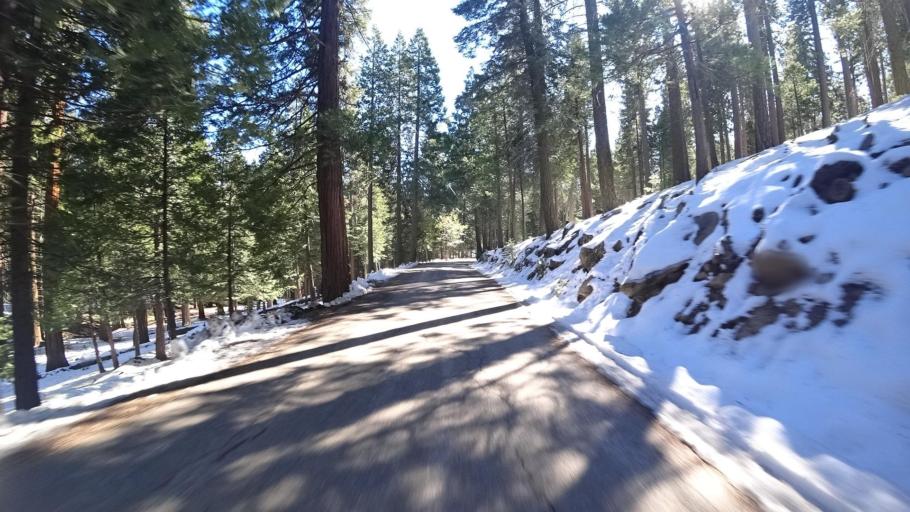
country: US
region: California
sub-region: Kern County
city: Alta Sierra
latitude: 35.7315
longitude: -118.5545
